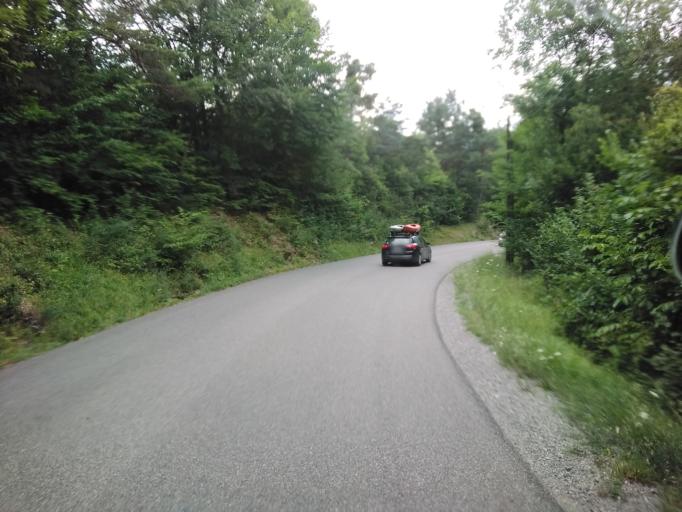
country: FR
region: Provence-Alpes-Cote d'Azur
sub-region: Departement des Alpes-de-Haute-Provence
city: Seyne-les-Alpes
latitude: 44.4492
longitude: 6.3937
